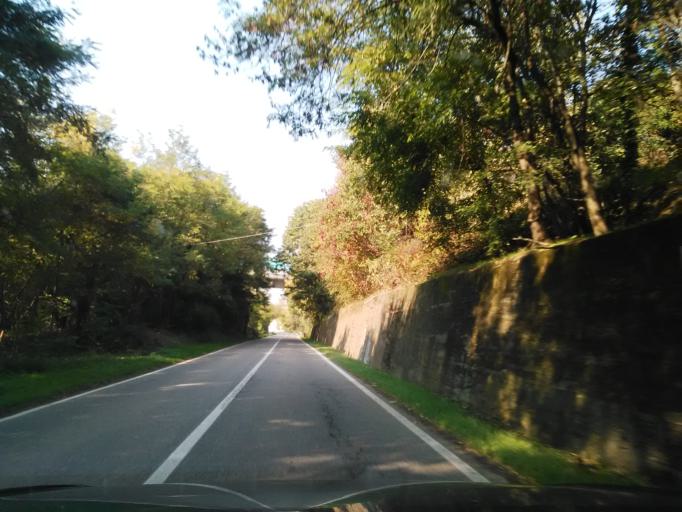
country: IT
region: Piedmont
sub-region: Provincia di Vercelli
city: Santhia
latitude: 45.3964
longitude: 8.1581
